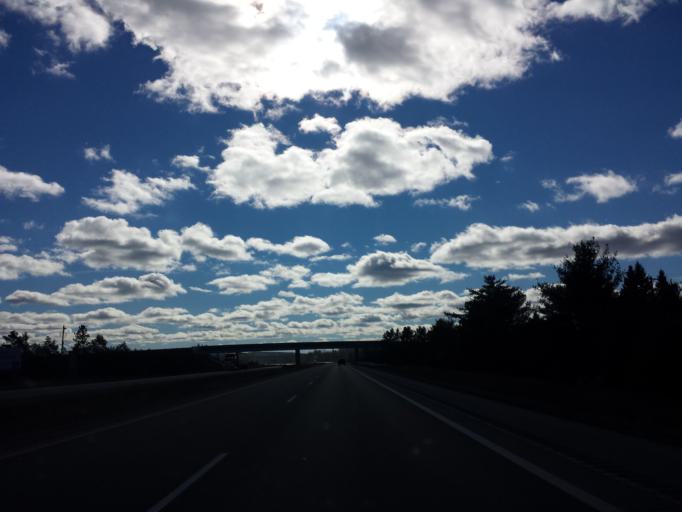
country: US
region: Michigan
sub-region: Cheboygan County
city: Indian River
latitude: 45.4127
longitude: -84.6044
